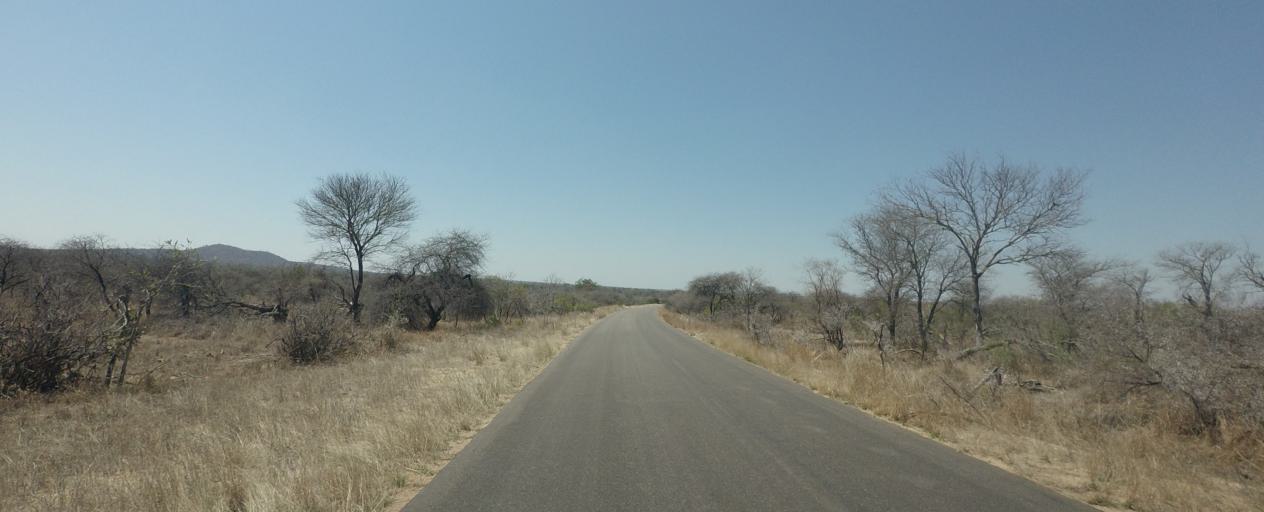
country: ZA
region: Limpopo
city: Thulamahashi
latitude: -24.4269
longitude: 31.5039
